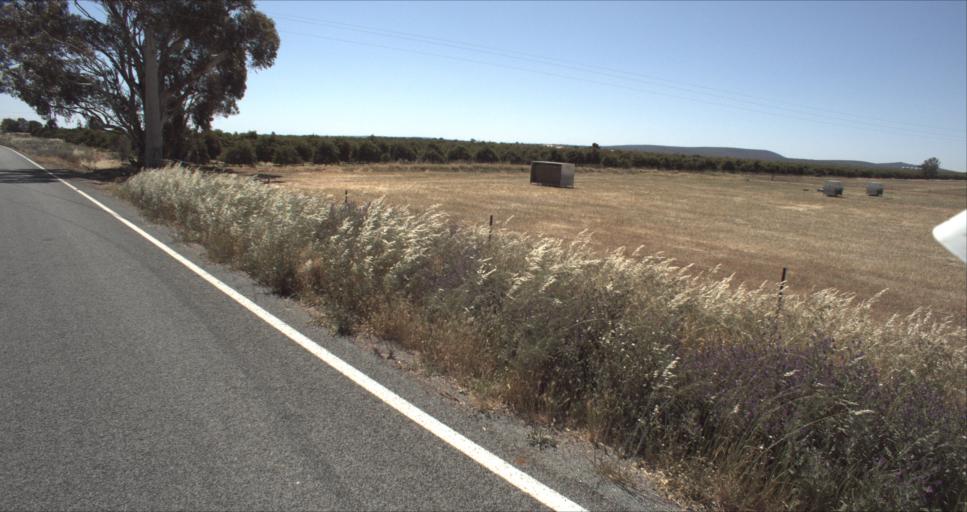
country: AU
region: New South Wales
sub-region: Leeton
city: Leeton
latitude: -34.5190
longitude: 146.4369
